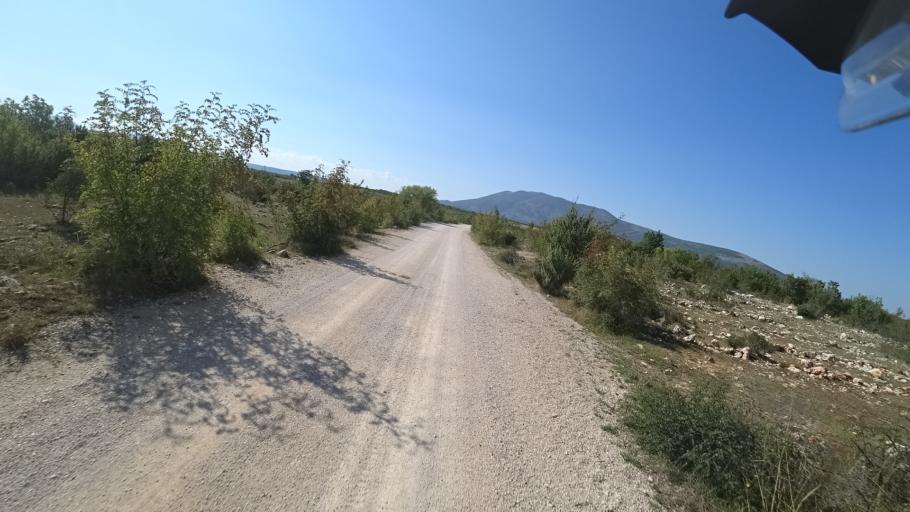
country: HR
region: Sibensko-Kniniska
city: Knin
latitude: 43.9952
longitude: 16.1934
